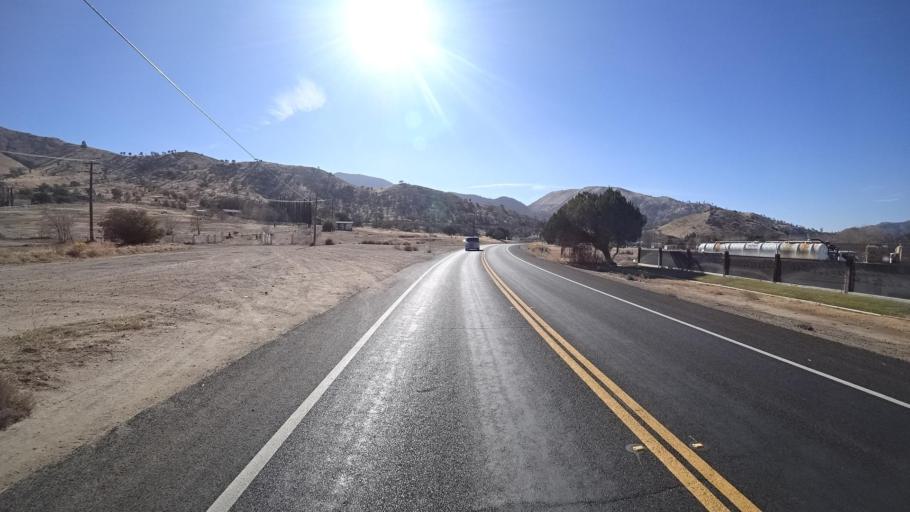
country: US
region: California
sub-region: Kern County
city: Bodfish
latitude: 35.6020
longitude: -118.4859
